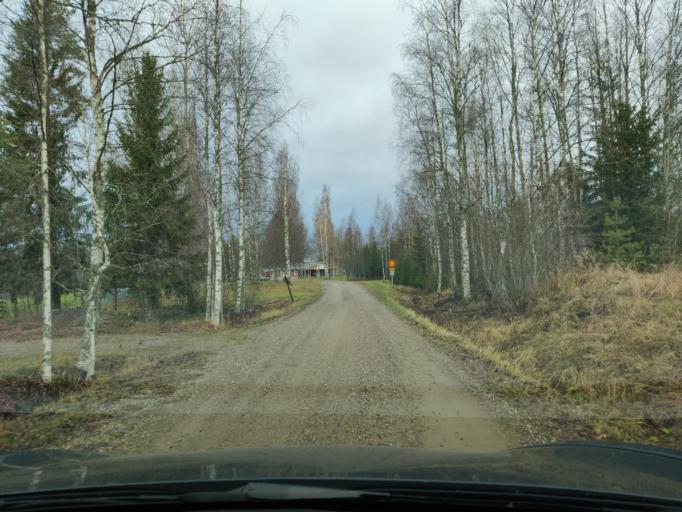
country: FI
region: Northern Savo
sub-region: Ylae-Savo
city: Kiuruvesi
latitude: 63.6400
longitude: 26.6549
